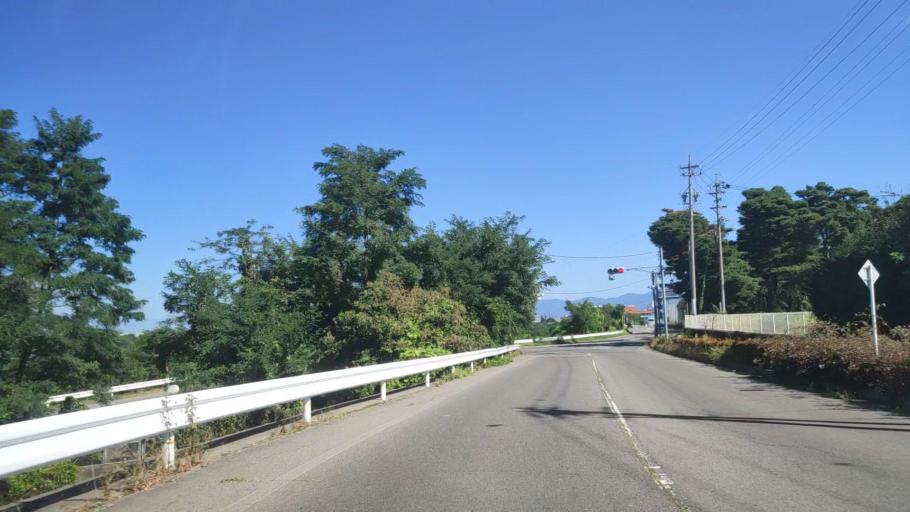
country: JP
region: Nagano
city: Shiojiri
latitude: 36.1633
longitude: 137.9451
